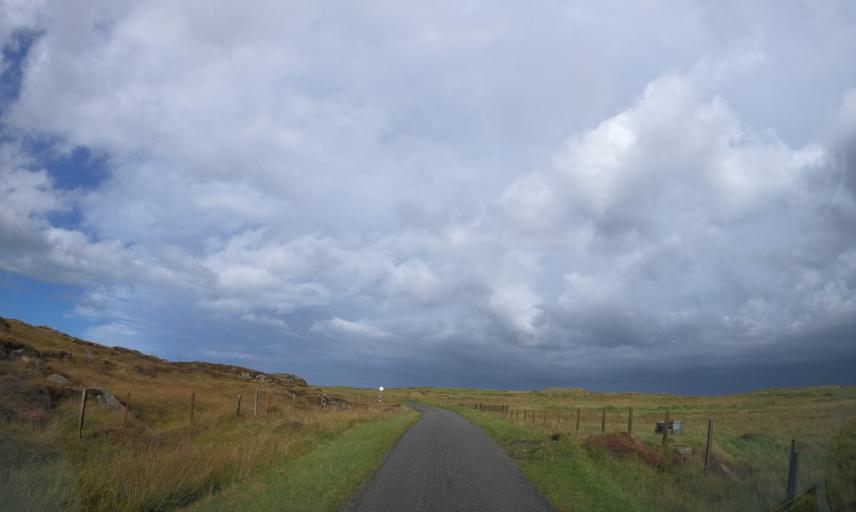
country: GB
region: Scotland
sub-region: Eilean Siar
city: Barra
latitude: 56.5212
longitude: -6.8416
